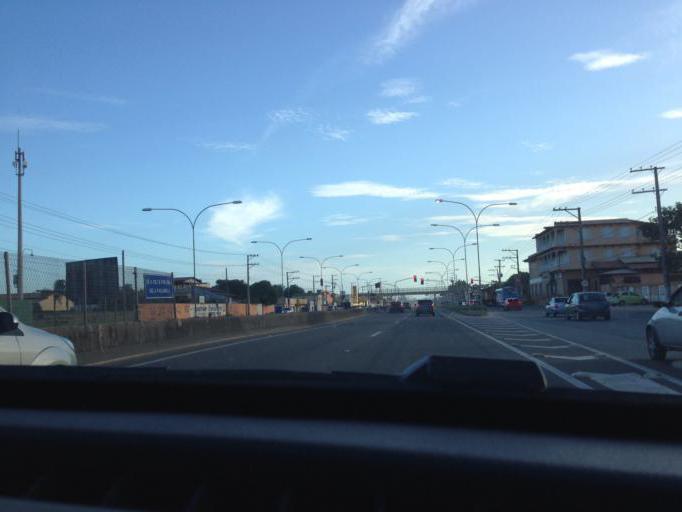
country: BR
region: Espirito Santo
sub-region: Vila Velha
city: Vila Velha
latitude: -20.4212
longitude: -40.3291
